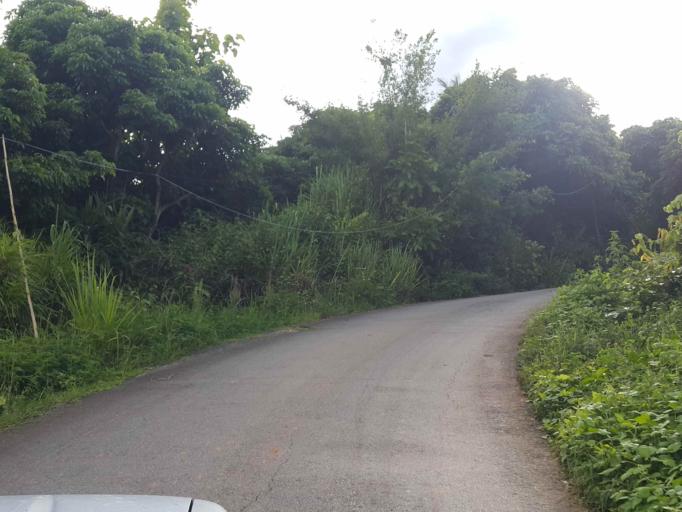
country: TH
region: Chiang Mai
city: Mae Chaem
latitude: 18.4823
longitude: 98.3794
